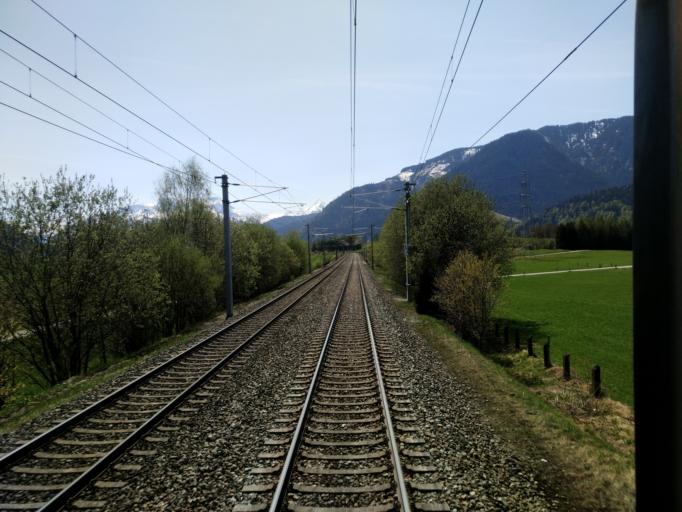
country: AT
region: Salzburg
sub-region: Politischer Bezirk Zell am See
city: Maishofen
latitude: 47.3767
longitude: 12.8166
